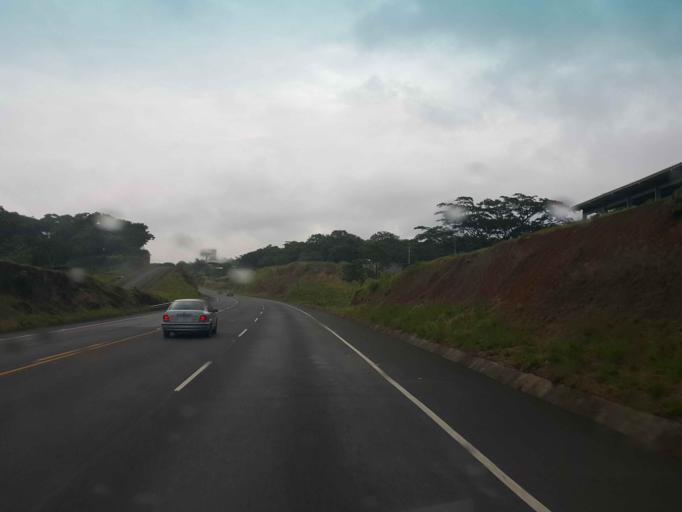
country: CR
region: Alajuela
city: Atenas
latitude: 9.9638
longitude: -84.3270
